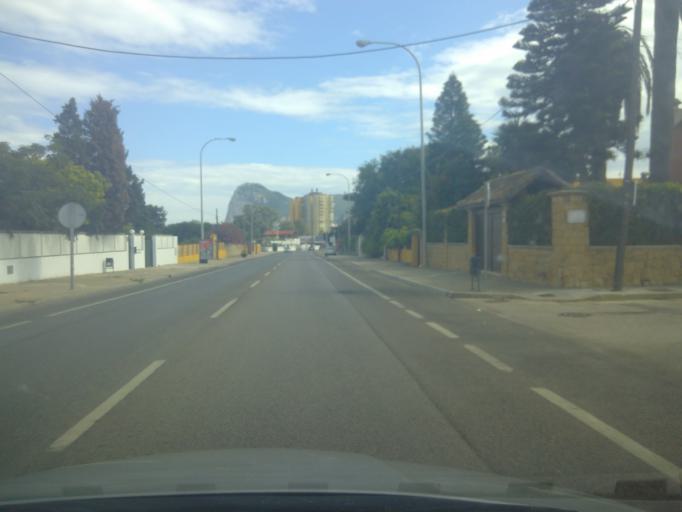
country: ES
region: Andalusia
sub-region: Provincia de Cadiz
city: La Linea de la Concepcion
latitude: 36.1732
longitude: -5.3726
